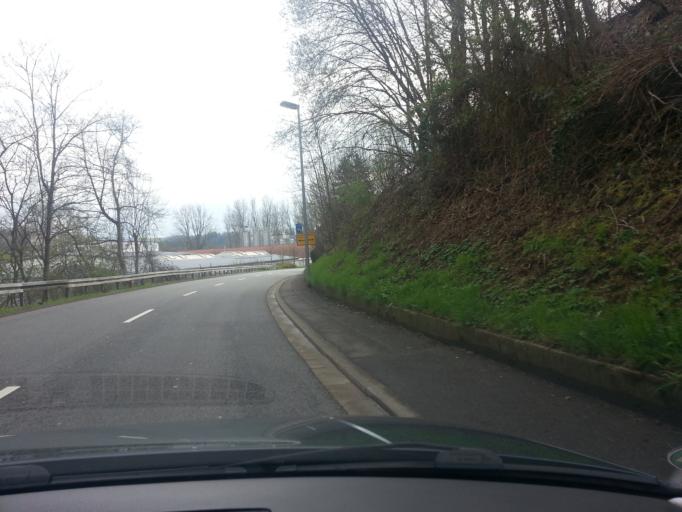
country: DE
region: Saarland
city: Homburg
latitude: 49.2871
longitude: 7.3106
